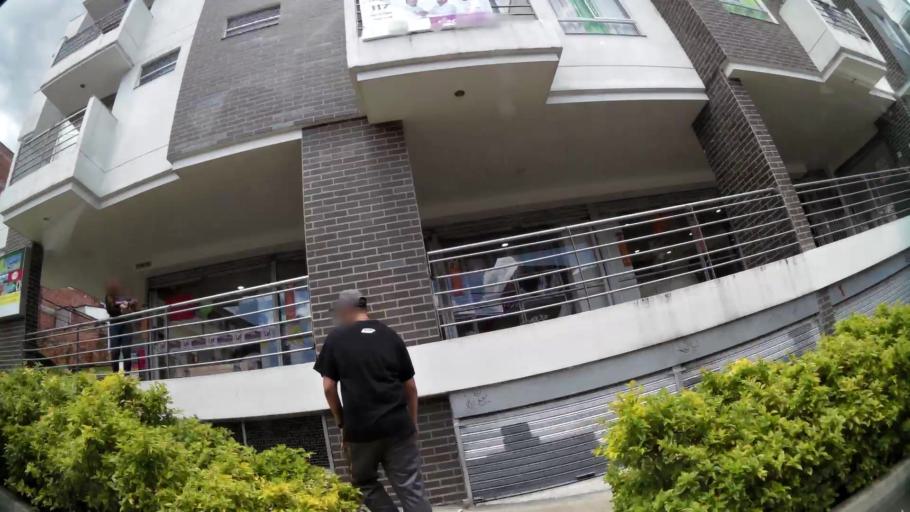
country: CO
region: Antioquia
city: La Estrella
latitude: 6.1592
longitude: -75.6423
